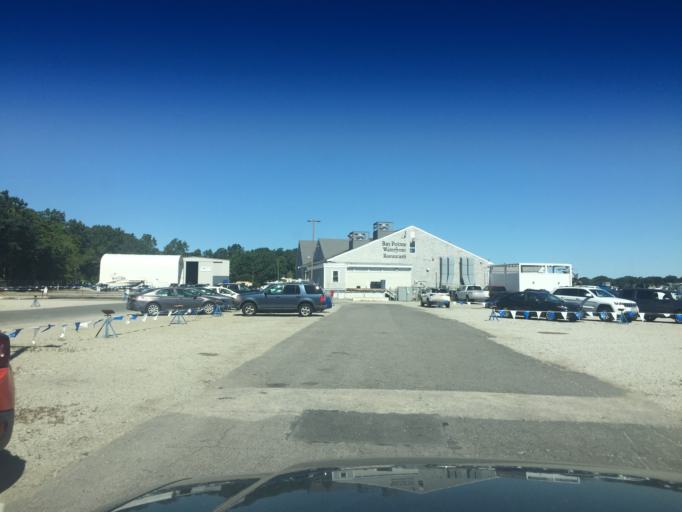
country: US
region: Massachusetts
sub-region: Norfolk County
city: Quincy
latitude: 42.2496
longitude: -70.9749
